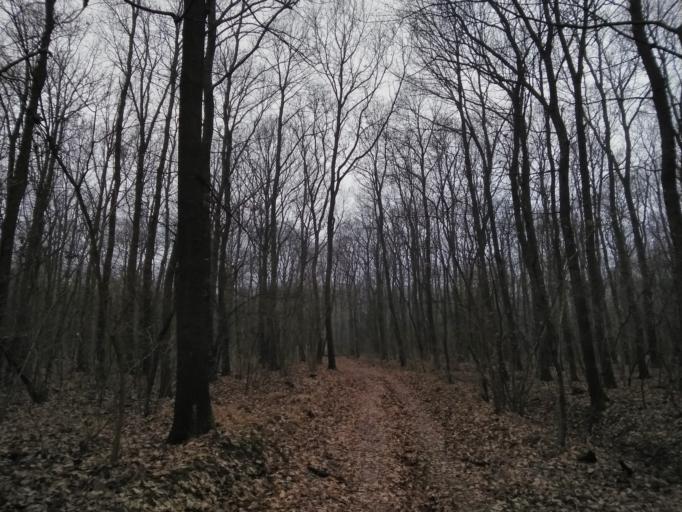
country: HU
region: Pest
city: Pilisszanto
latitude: 47.6444
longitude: 18.8631
